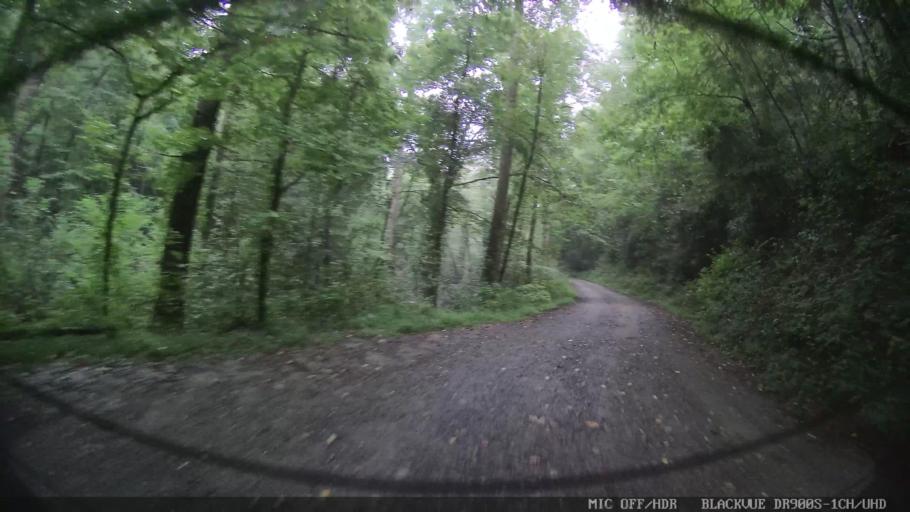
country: US
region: Georgia
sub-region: Gilmer County
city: Ellijay
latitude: 34.8115
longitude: -84.5592
